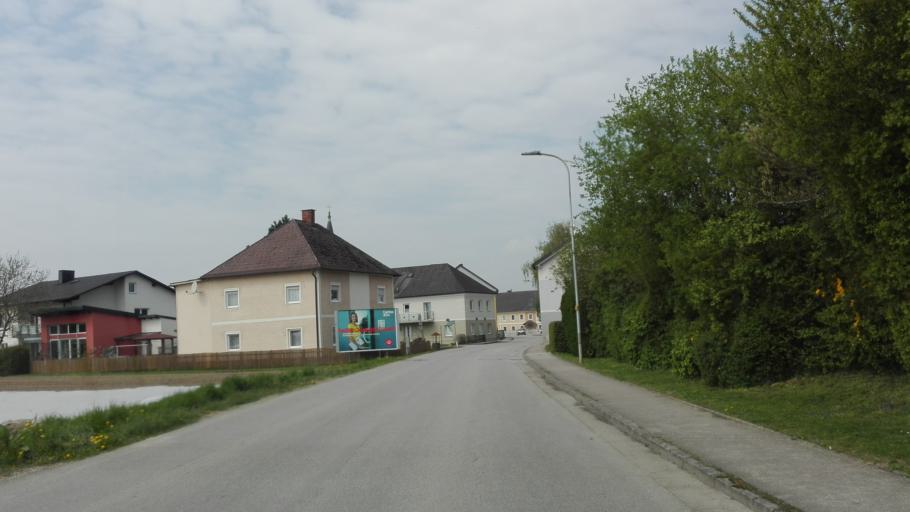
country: AT
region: Upper Austria
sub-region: Politischer Bezirk Perg
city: Perg
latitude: 48.2245
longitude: 14.6116
